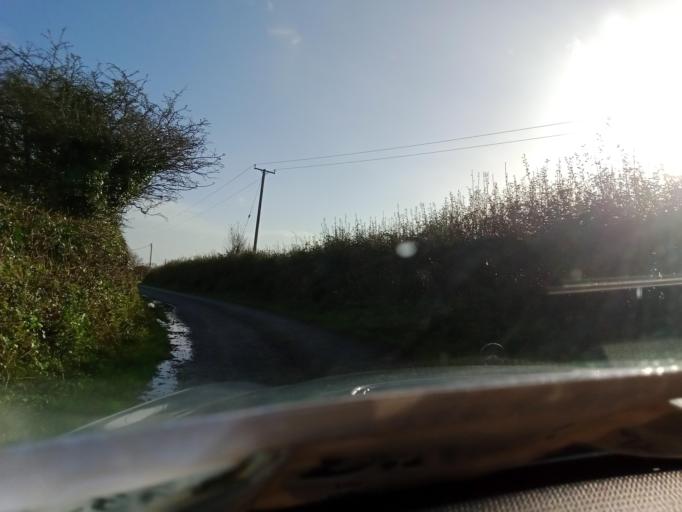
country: IE
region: Leinster
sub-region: Kilkenny
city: Mooncoin
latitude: 52.3135
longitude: -7.2809
